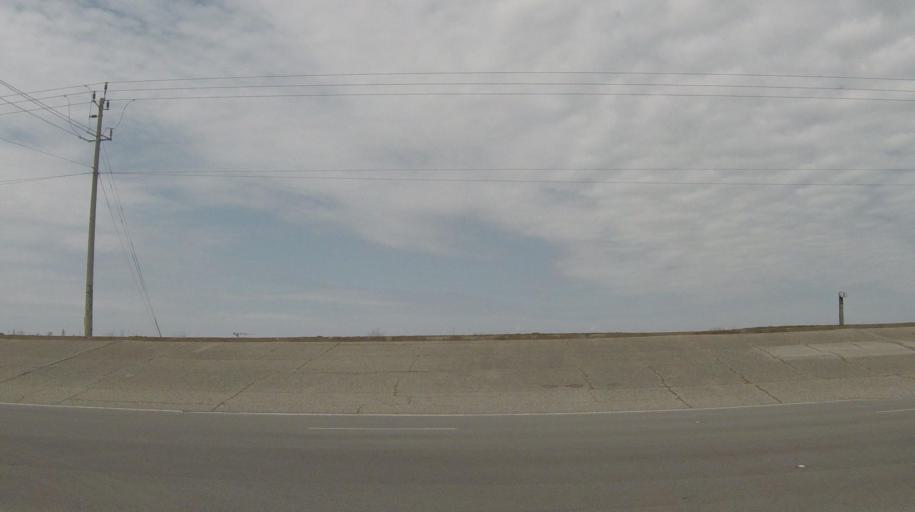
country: US
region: Texas
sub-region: Galveston County
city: Galveston
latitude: 29.3162
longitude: -94.7632
